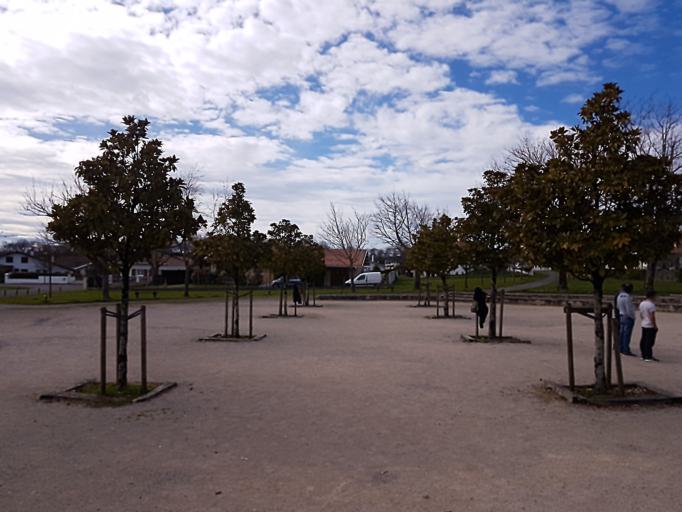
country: FR
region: Aquitaine
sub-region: Departement des Landes
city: Saint-Martin-de-Seignanx
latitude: 43.5415
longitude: -1.3878
